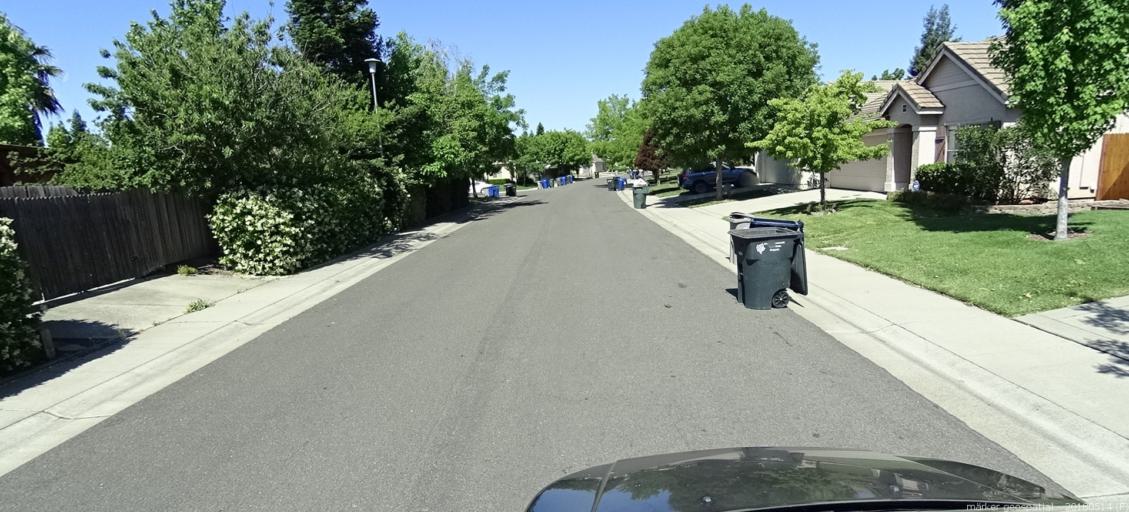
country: US
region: California
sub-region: Yolo County
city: West Sacramento
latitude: 38.6347
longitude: -121.5272
